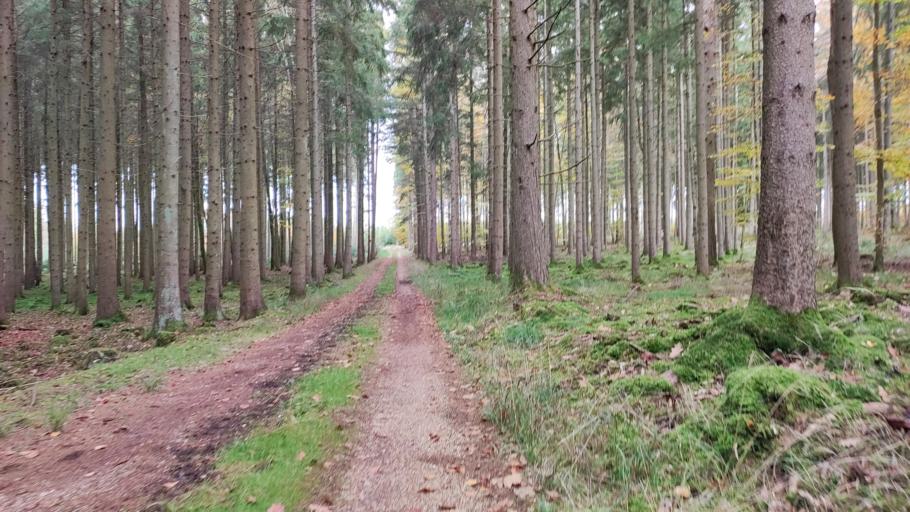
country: DE
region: Bavaria
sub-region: Swabia
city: Munsterhausen
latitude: 48.3247
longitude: 10.4966
